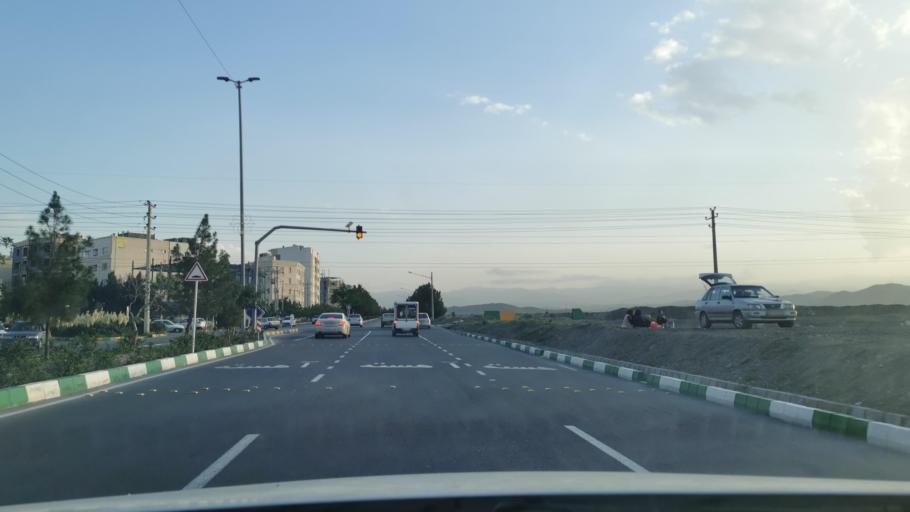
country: IR
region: Razavi Khorasan
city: Mashhad
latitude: 36.3912
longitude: 59.4701
